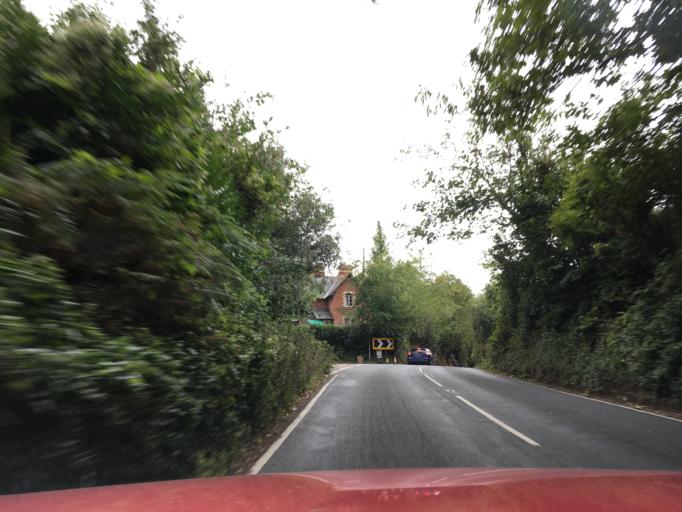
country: GB
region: England
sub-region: Devon
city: Exminster
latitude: 50.6553
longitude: -3.4826
